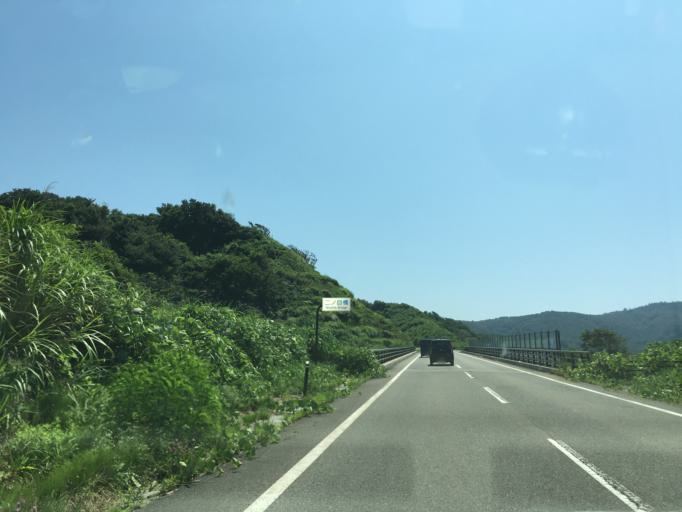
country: JP
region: Akita
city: Tenno
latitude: 39.9587
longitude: 139.7208
